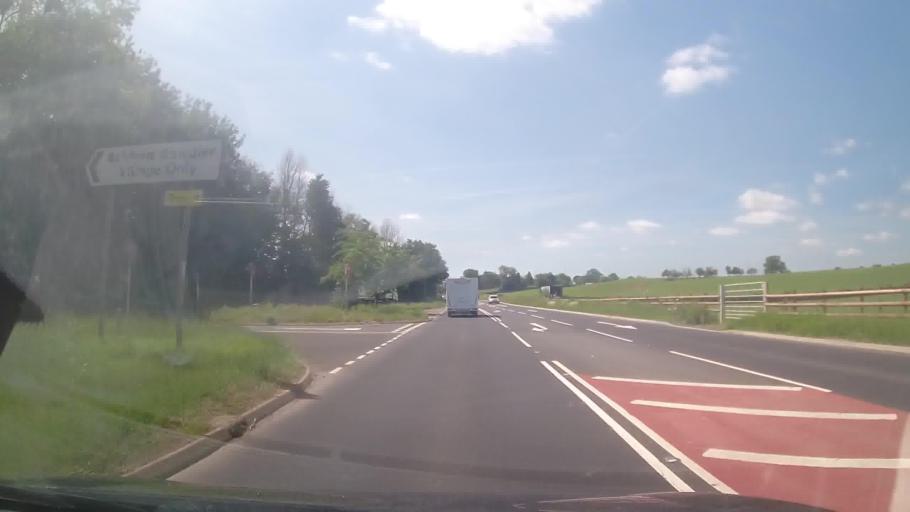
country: GB
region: England
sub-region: Shropshire
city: Ludlow
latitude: 52.3321
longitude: -2.7128
